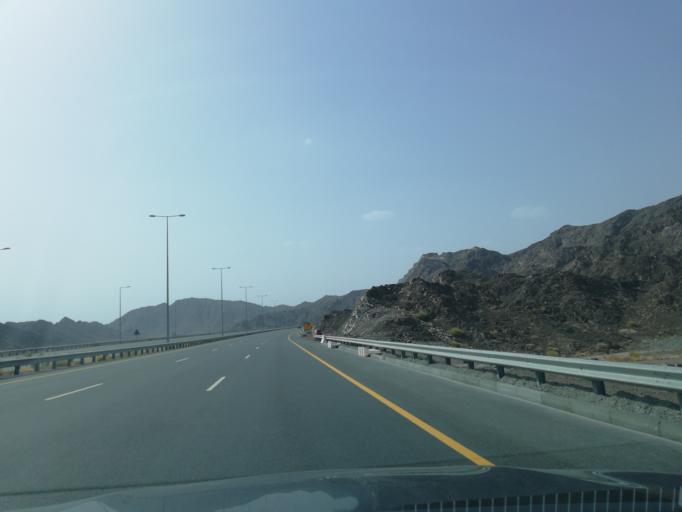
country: OM
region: Muhafazat ad Dakhiliyah
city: Sufalat Sama'il
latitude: 22.9760
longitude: 58.2361
